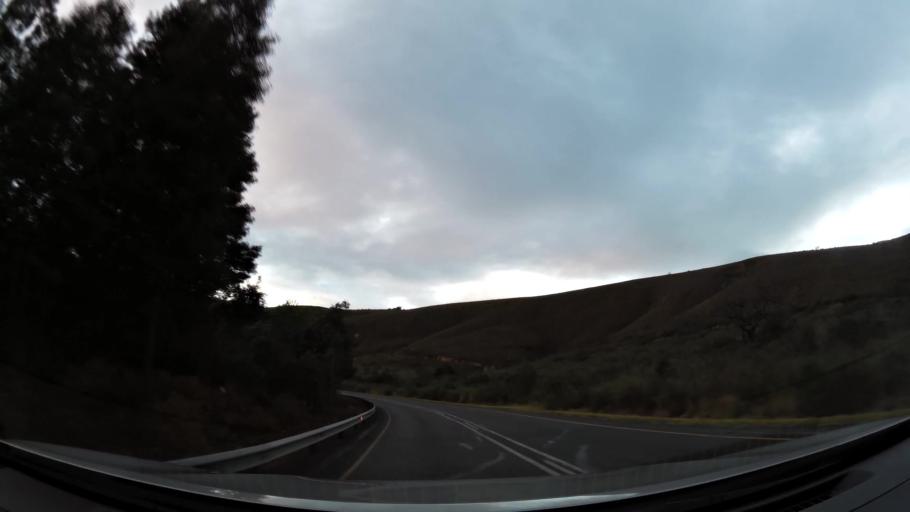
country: ZA
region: Western Cape
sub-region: Overberg District Municipality
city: Swellendam
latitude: -33.9896
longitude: 20.7153
